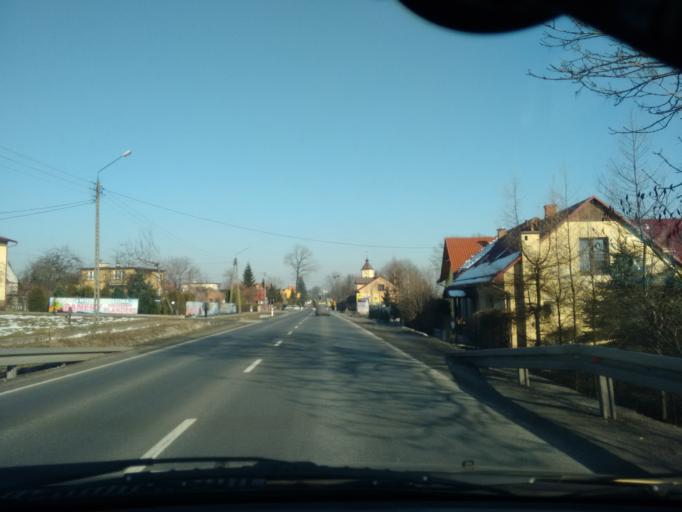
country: PL
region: Lesser Poland Voivodeship
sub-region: Powiat wadowicki
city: Inwald
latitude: 49.8620
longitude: 19.3887
